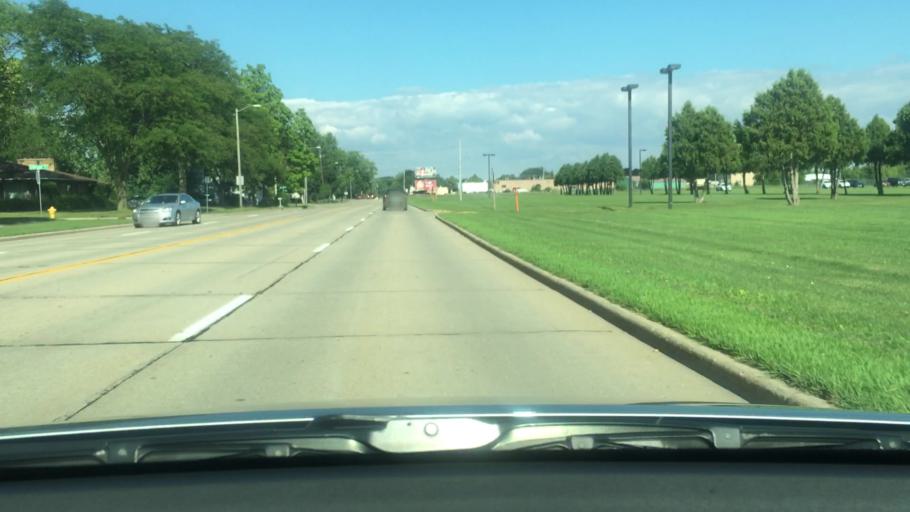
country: US
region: Wisconsin
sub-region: Winnebago County
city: Oshkosh
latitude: 43.9958
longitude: -88.5519
